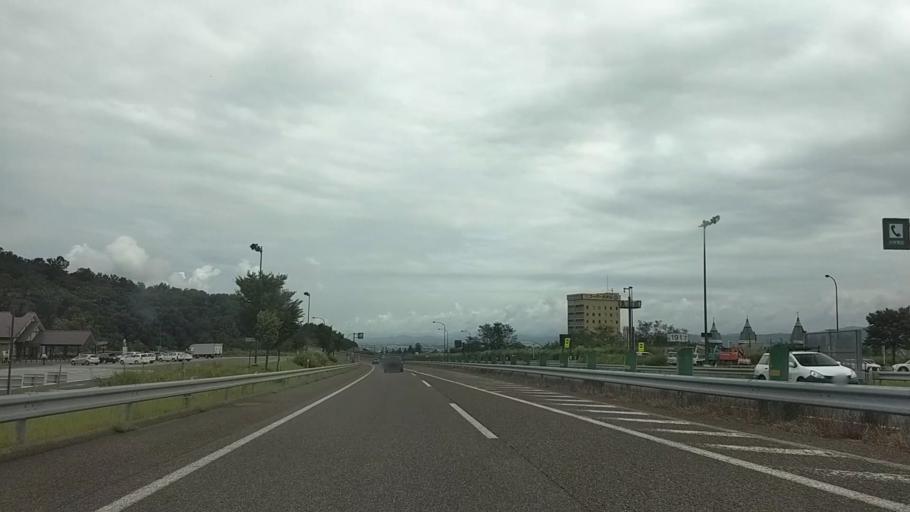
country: JP
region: Niigata
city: Arai
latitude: 37.0269
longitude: 138.2245
